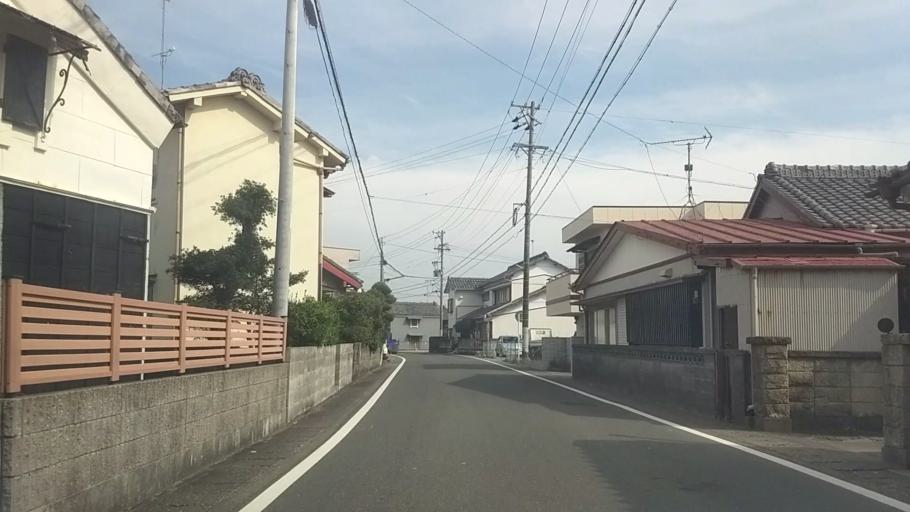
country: JP
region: Shizuoka
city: Kosai-shi
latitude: 34.6977
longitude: 137.6282
